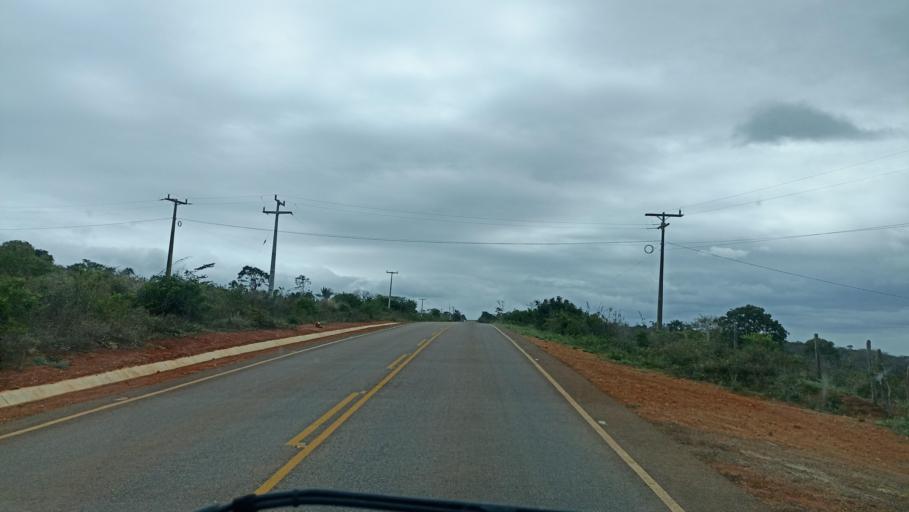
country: BR
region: Bahia
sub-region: Andarai
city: Vera Cruz
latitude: -12.9963
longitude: -40.9959
